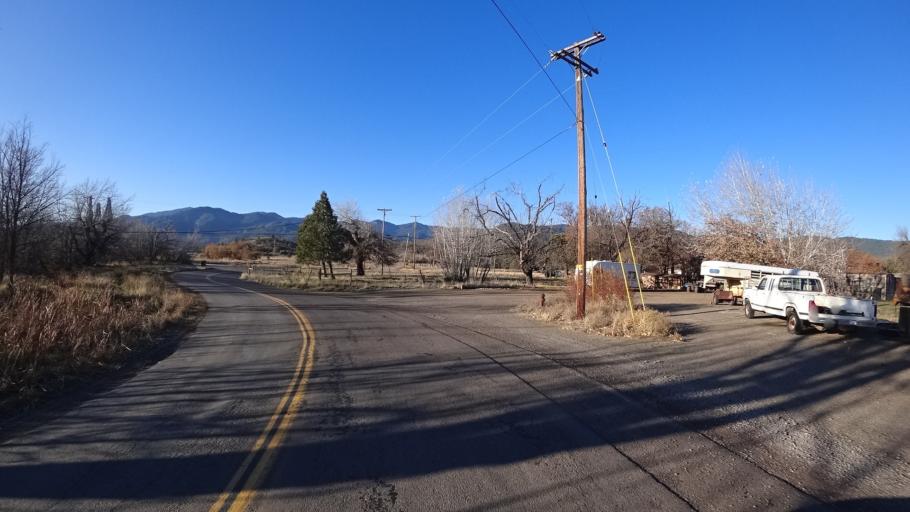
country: US
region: Oregon
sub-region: Jackson County
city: Ashland
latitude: 41.9961
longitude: -122.6236
